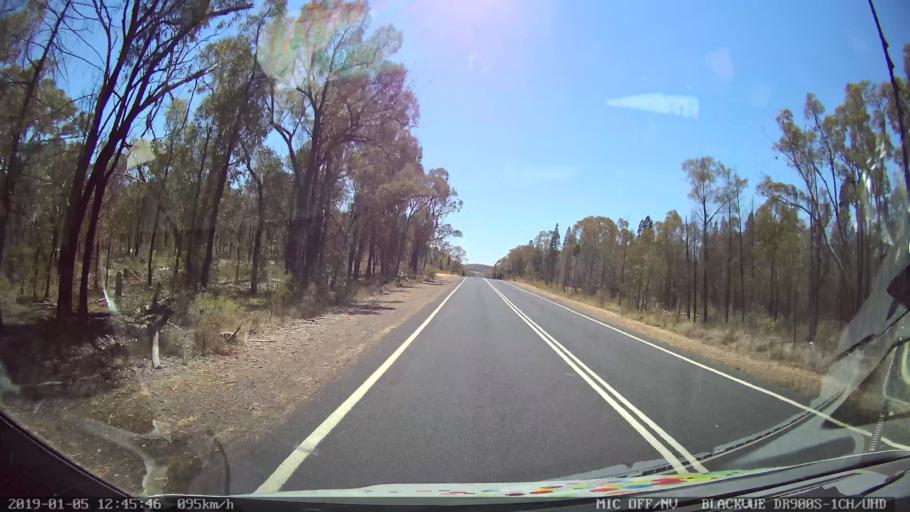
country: AU
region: New South Wales
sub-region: Warrumbungle Shire
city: Coonabarabran
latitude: -31.1246
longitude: 149.5541
